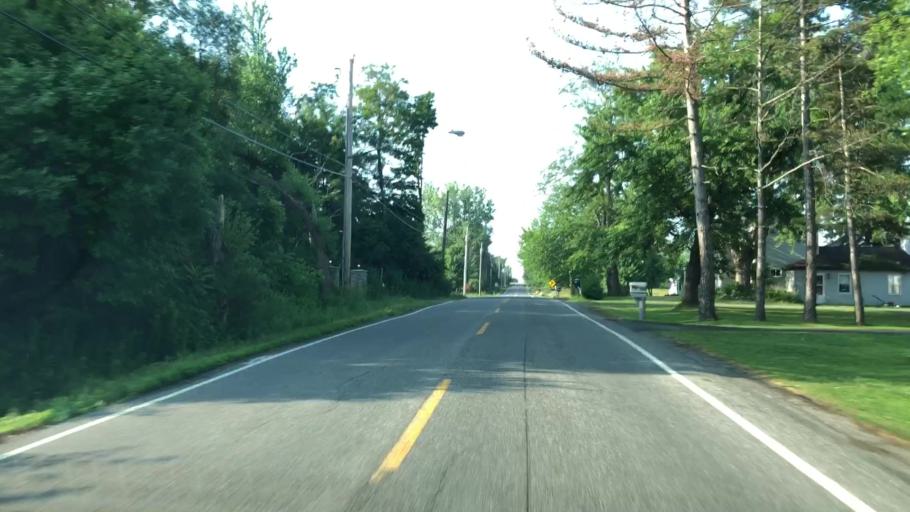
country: US
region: New York
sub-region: Erie County
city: Depew
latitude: 42.8490
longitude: -78.6923
